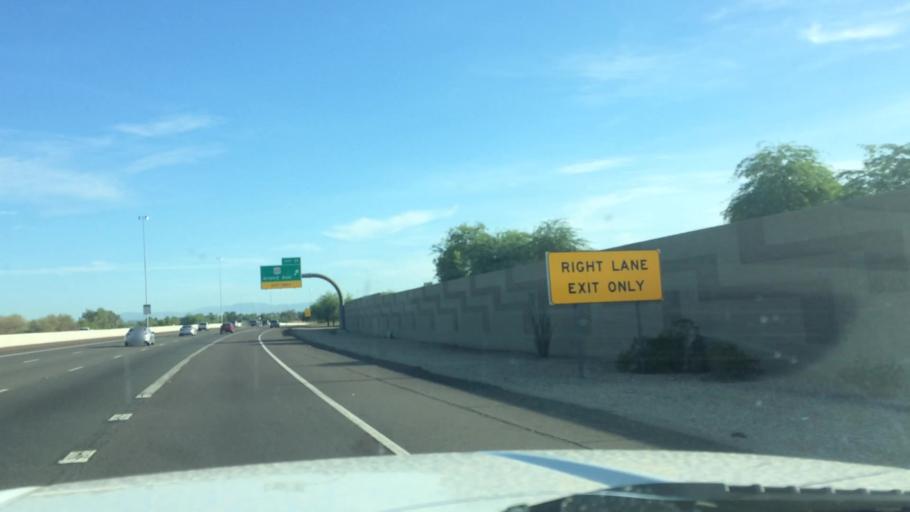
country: US
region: Arizona
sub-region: Maricopa County
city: Sun City
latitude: 33.5875
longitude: -112.2597
